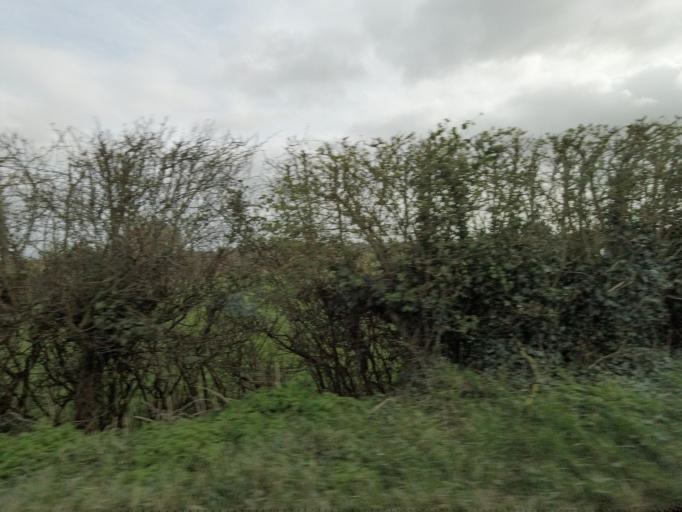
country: IE
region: Leinster
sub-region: Kildare
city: Kilcullen
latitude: 53.1441
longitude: -6.7310
